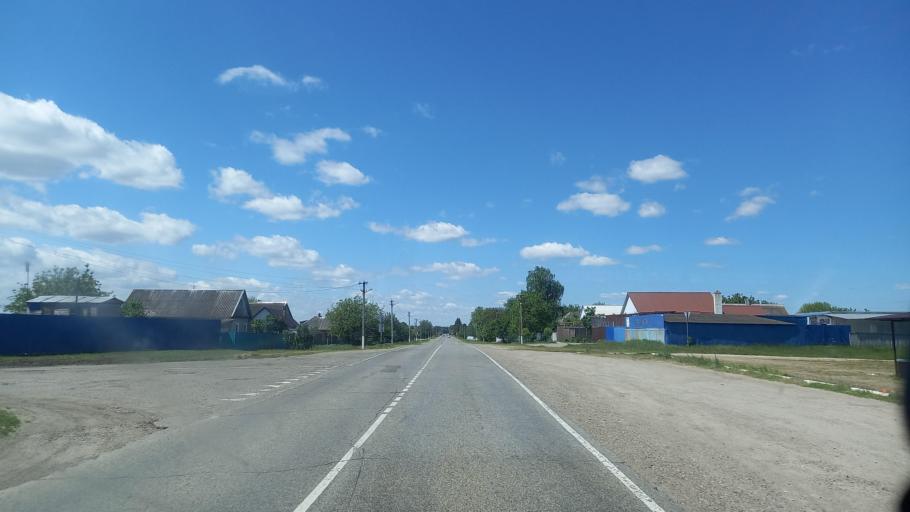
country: RU
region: Krasnodarskiy
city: Kazanskaya
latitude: 45.3637
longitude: 40.3909
